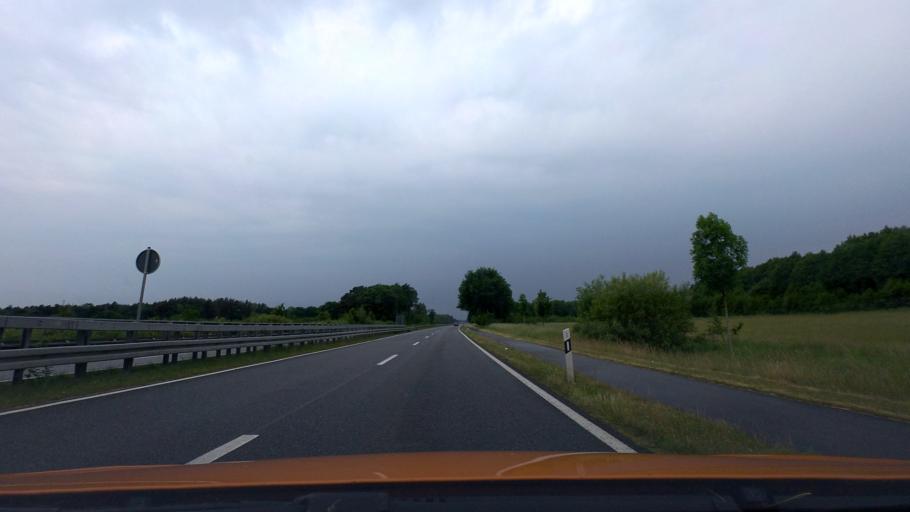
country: DE
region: Lower Saxony
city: Neustadt am Rubenberge
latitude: 52.5263
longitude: 9.4421
